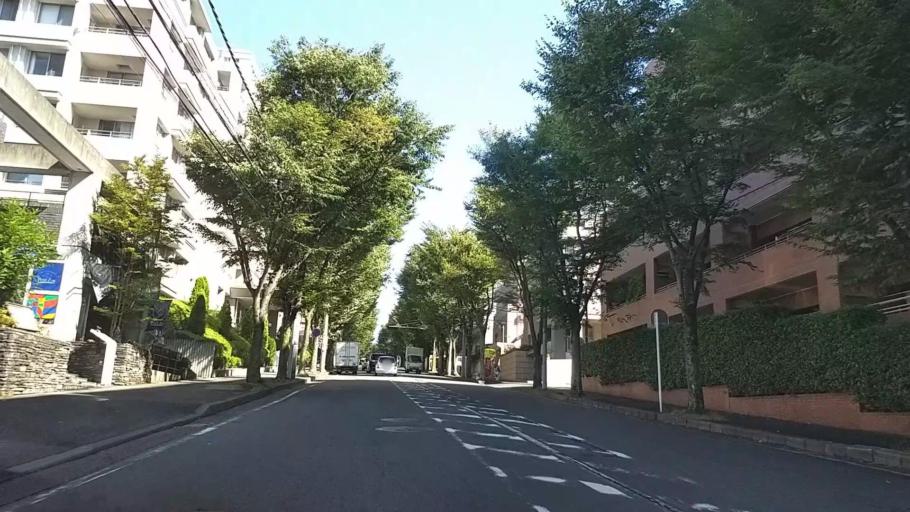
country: JP
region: Tokyo
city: Chofugaoka
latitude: 35.5719
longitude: 139.5549
